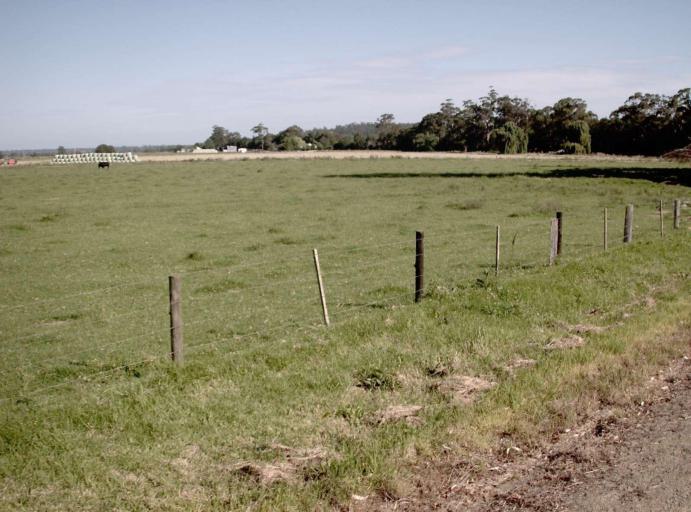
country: AU
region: Victoria
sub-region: East Gippsland
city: Lakes Entrance
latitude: -37.7360
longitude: 148.5047
